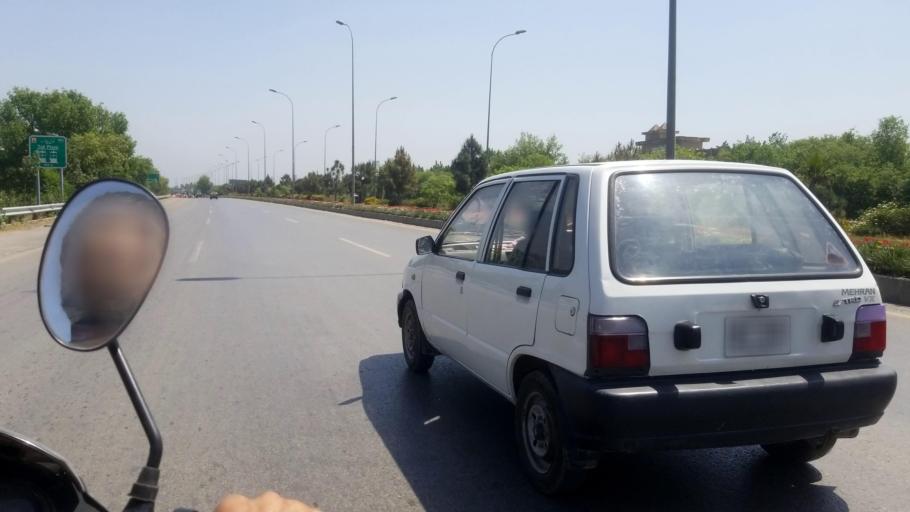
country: PK
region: Khyber Pakhtunkhwa
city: Peshawar
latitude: 34.0288
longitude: 71.6591
